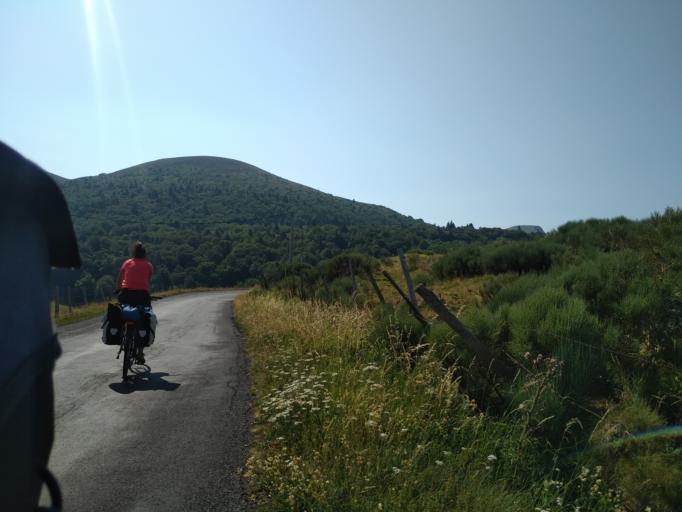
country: FR
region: Auvergne
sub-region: Departement du Puy-de-Dome
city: Mont-Dore
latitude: 45.5754
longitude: 2.8175
